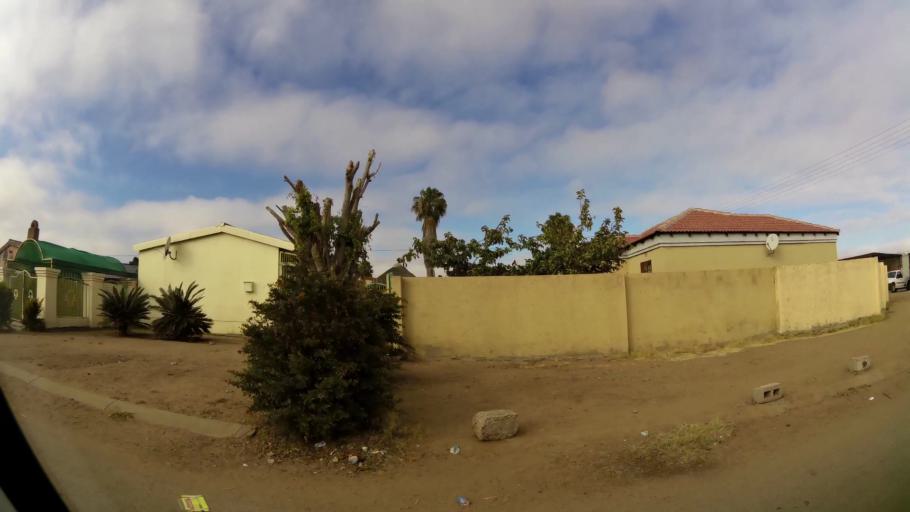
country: ZA
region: Limpopo
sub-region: Capricorn District Municipality
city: Polokwane
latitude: -23.8450
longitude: 29.3809
